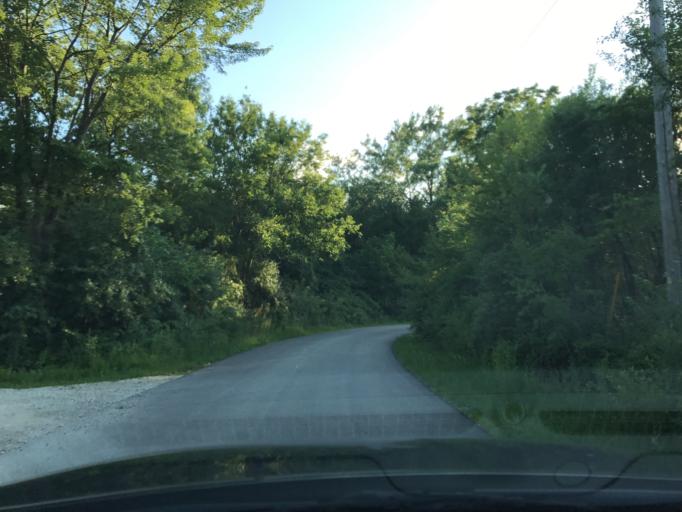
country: US
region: Illinois
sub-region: DuPage County
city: Naperville
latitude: 41.7608
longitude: -88.1604
